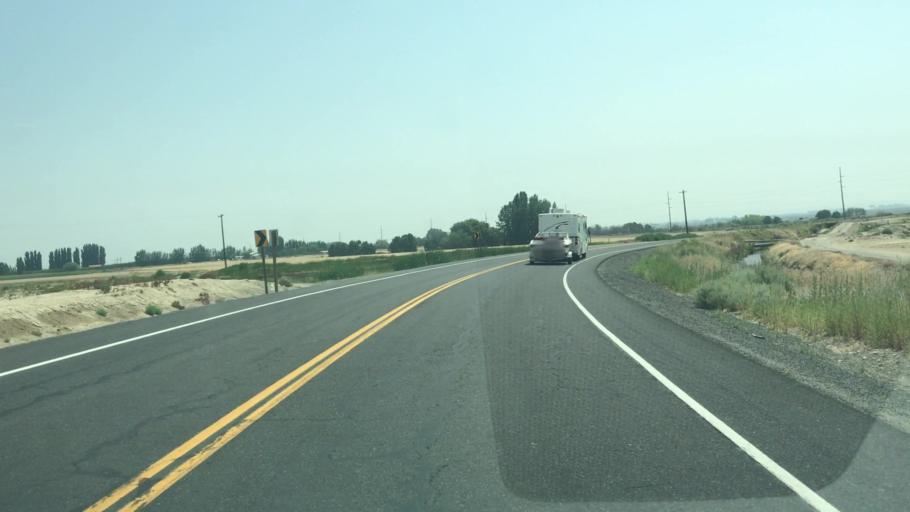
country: US
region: Washington
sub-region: Grant County
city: Quincy
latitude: 47.1634
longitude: -119.9200
